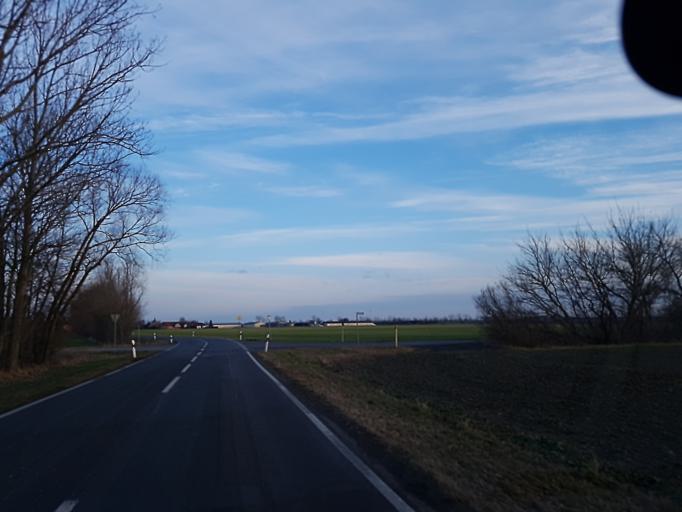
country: DE
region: Brandenburg
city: Juterbog
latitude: 51.9217
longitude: 13.0716
